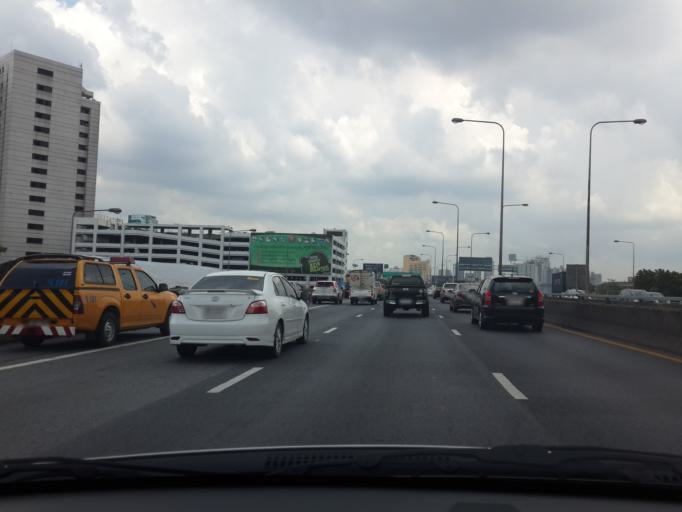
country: TH
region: Bangkok
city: Khlong Toei
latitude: 13.7117
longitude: 100.5663
